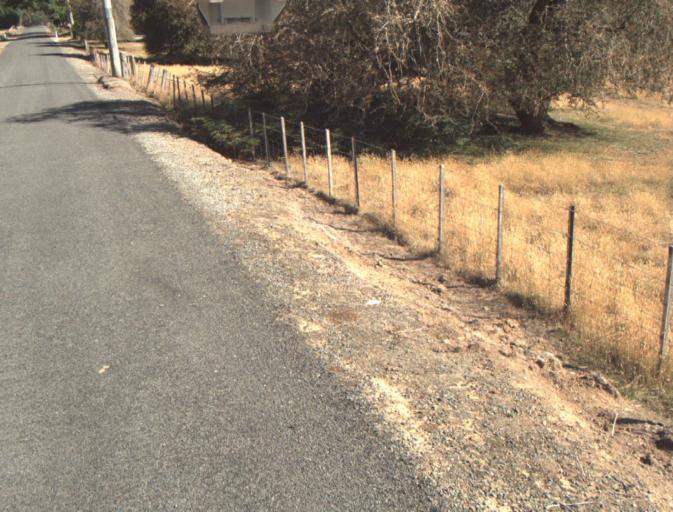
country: AU
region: Tasmania
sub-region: Dorset
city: Scottsdale
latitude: -41.2963
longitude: 147.3536
